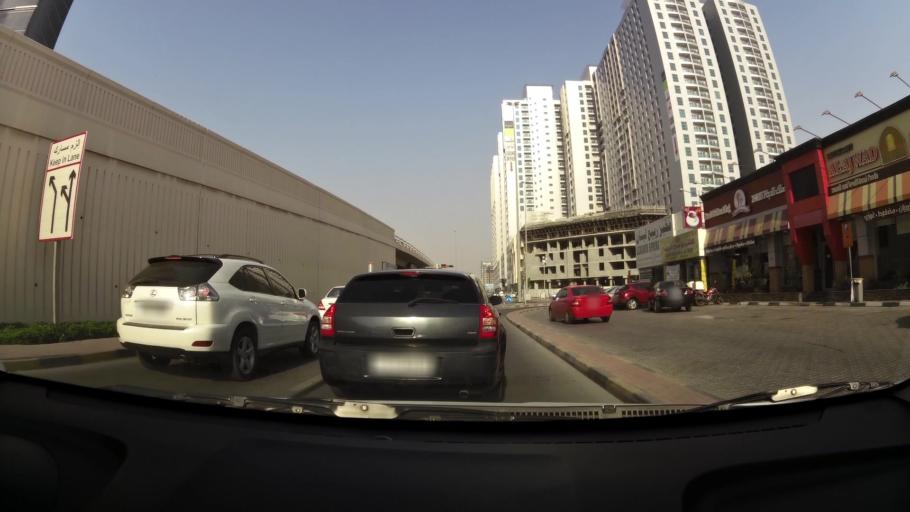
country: AE
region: Ajman
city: Ajman
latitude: 25.3917
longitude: 55.4393
